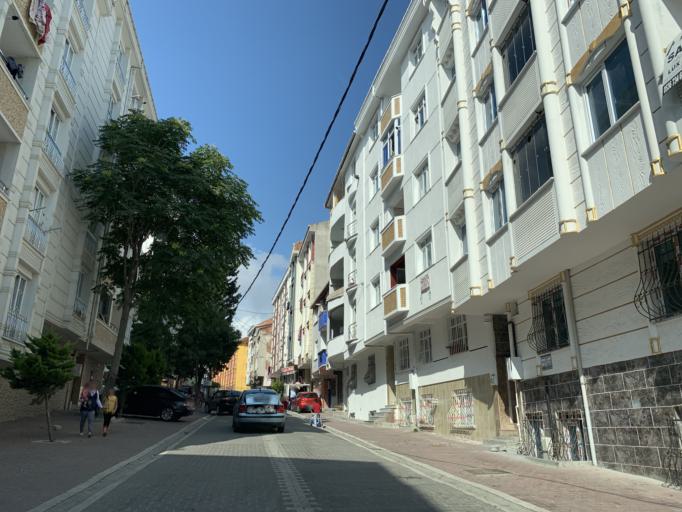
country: TR
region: Istanbul
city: Esenyurt
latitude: 41.0350
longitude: 28.6702
